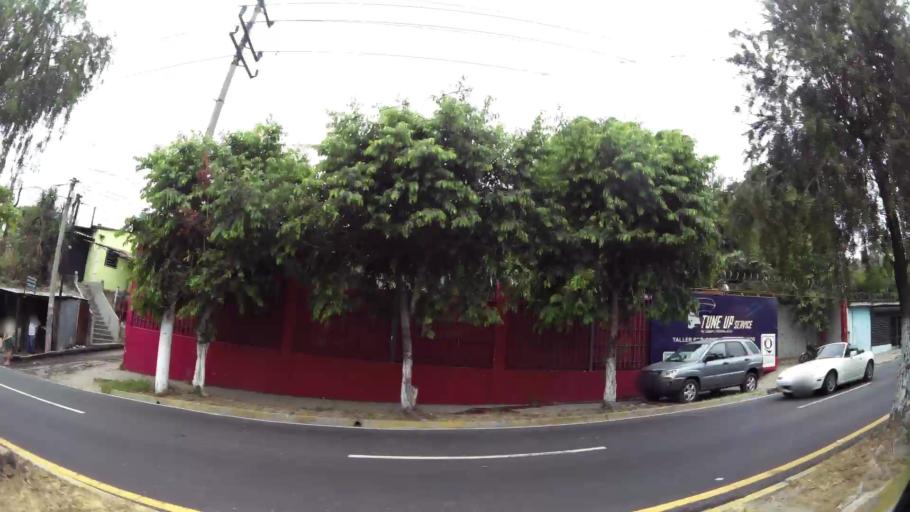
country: SV
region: San Salvador
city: Mejicanos
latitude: 13.7158
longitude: -89.2308
